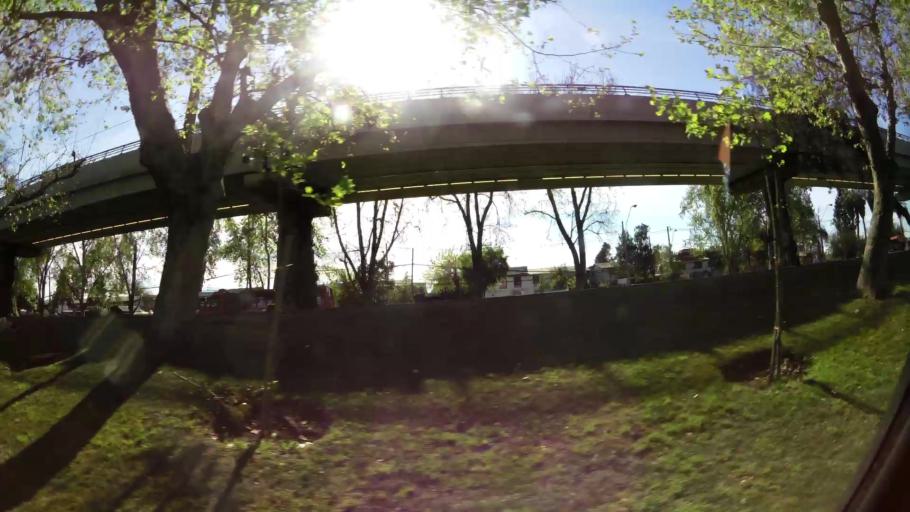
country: CL
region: Santiago Metropolitan
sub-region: Provincia de Santiago
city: Lo Prado
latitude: -33.4731
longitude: -70.7380
